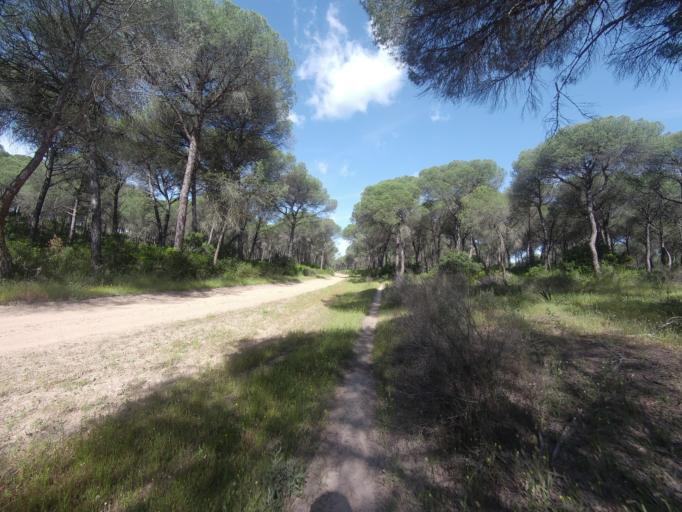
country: ES
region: Andalusia
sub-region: Provincia de Huelva
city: Aljaraque
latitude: 37.2354
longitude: -7.0528
